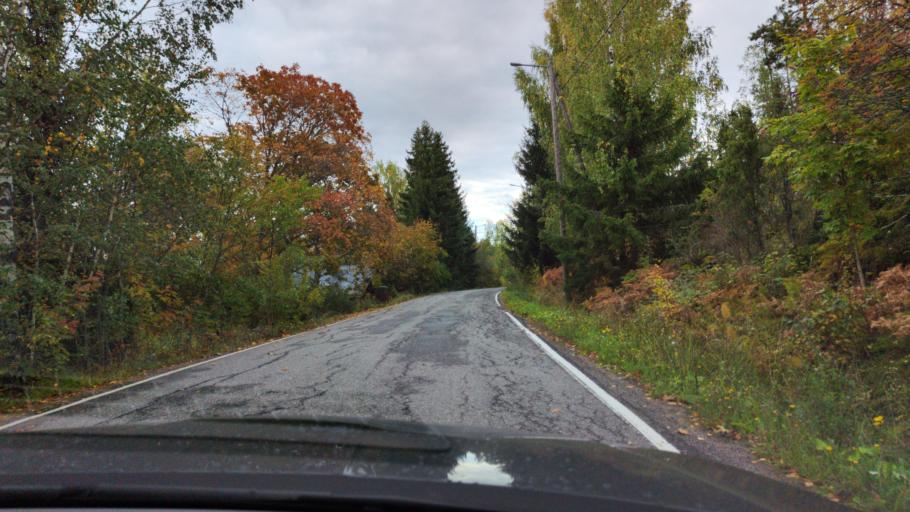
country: FI
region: Varsinais-Suomi
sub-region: Aboland-Turunmaa
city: Pargas
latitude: 60.3631
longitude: 22.2788
